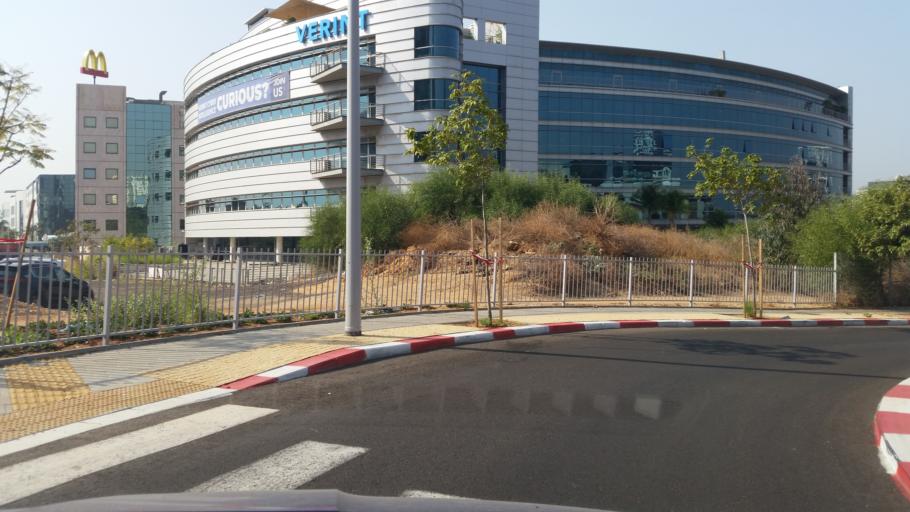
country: IL
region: Tel Aviv
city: Herzliyya
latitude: 32.1624
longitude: 34.8117
